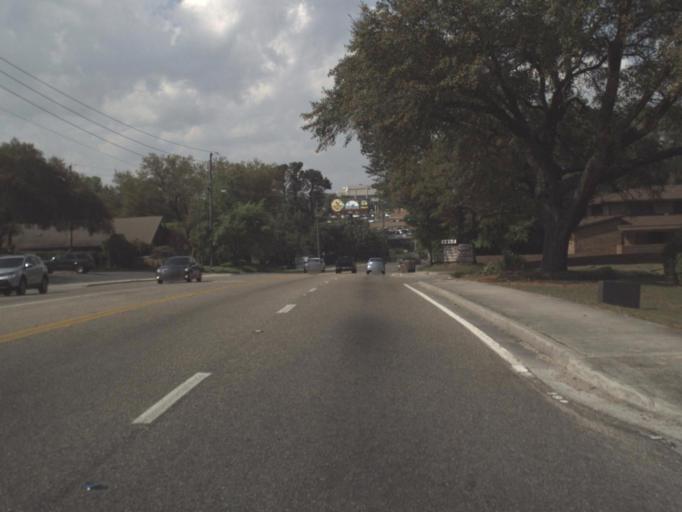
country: US
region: Florida
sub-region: Escambia County
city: Brent
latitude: 30.4691
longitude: -87.2138
